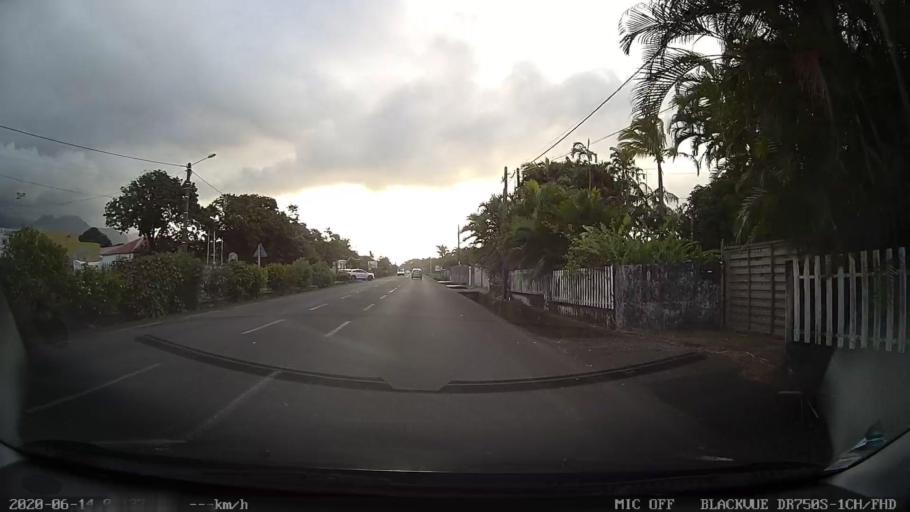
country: RE
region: Reunion
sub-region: Reunion
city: Bras-Panon
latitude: -21.0024
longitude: 55.6910
